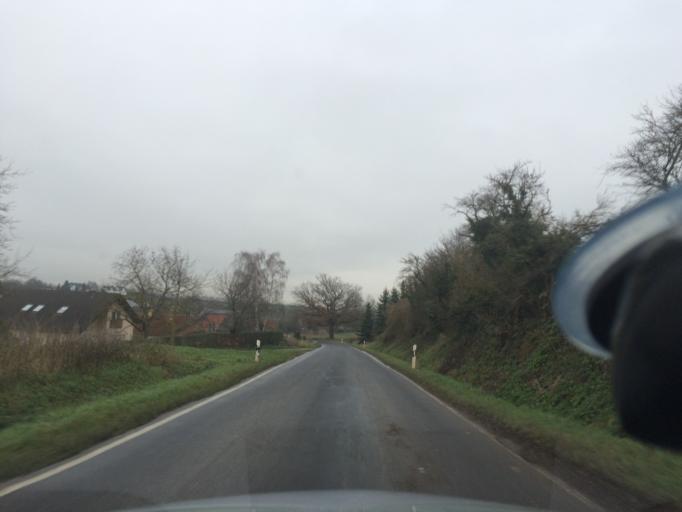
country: DE
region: Rheinland-Pfalz
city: Gabsheim
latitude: 49.8253
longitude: 8.1736
